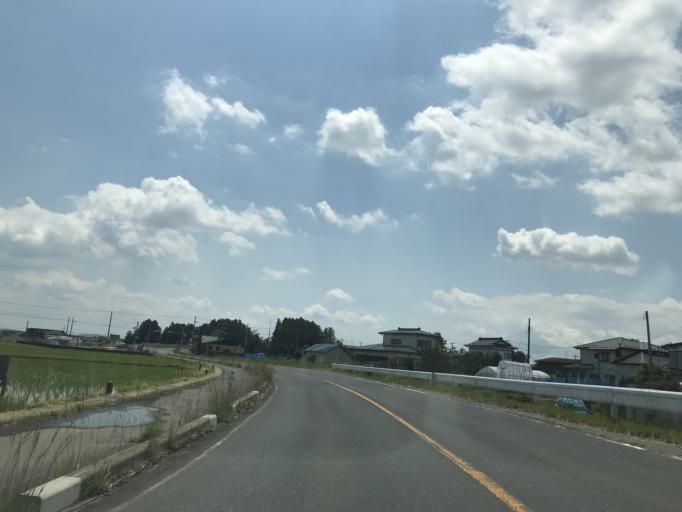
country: JP
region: Miyagi
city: Kogota
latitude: 38.5322
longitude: 141.0551
